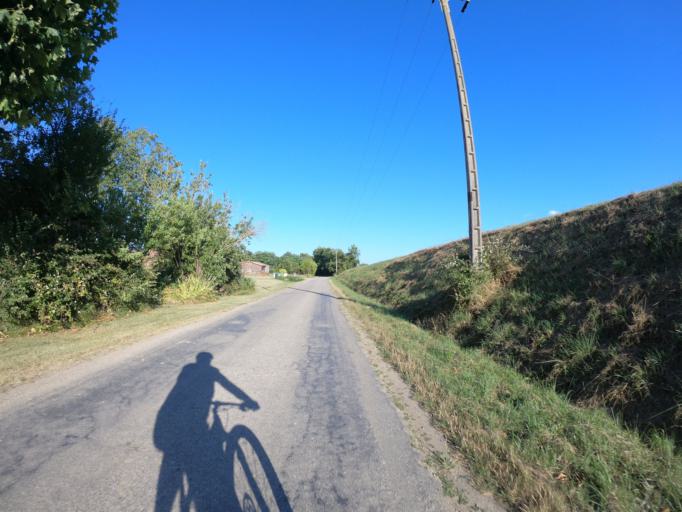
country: FR
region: Midi-Pyrenees
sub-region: Departement de l'Ariege
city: La Tour-du-Crieu
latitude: 43.0956
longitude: 1.7365
